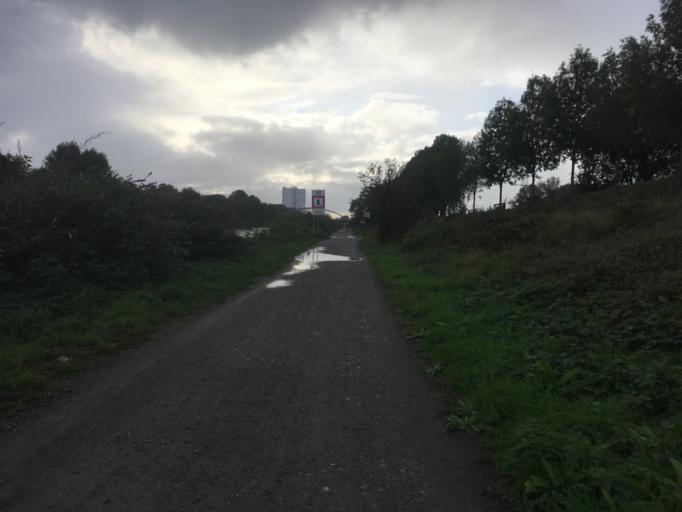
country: DE
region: North Rhine-Westphalia
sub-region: Regierungsbezirk Dusseldorf
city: Oberhausen
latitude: 51.4950
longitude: 6.8977
